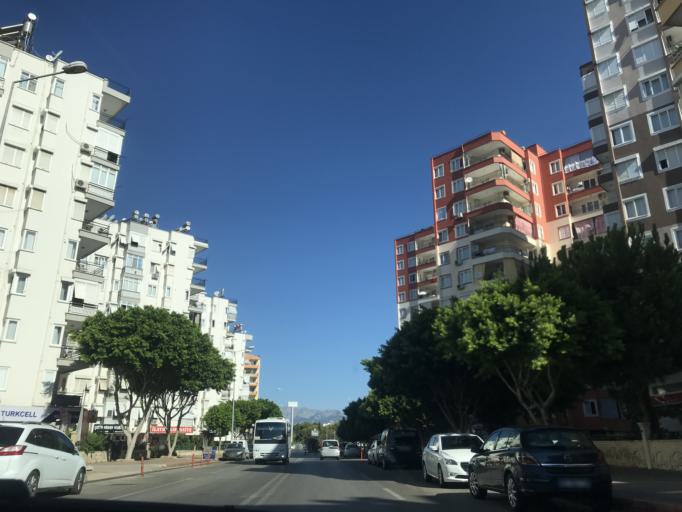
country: TR
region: Antalya
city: Antalya
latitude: 36.8940
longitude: 30.6299
